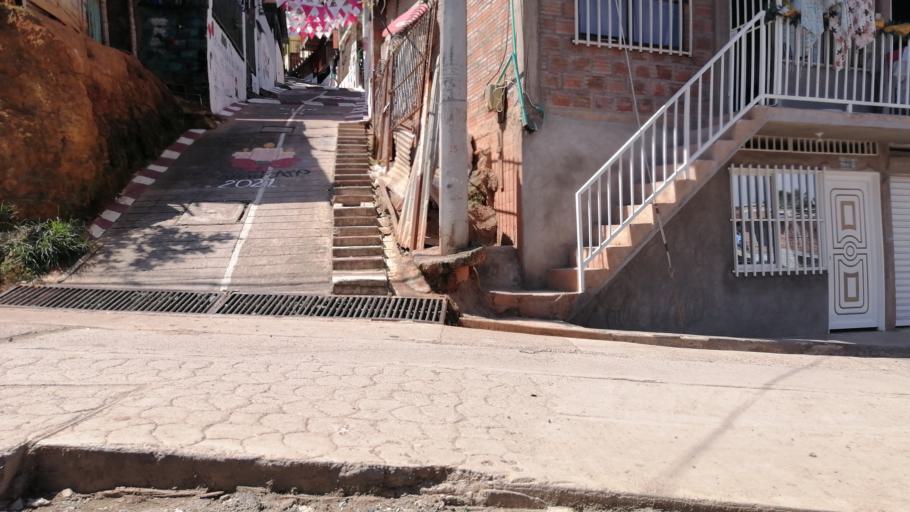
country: CO
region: Valle del Cauca
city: Cali
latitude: 3.3788
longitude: -76.5588
